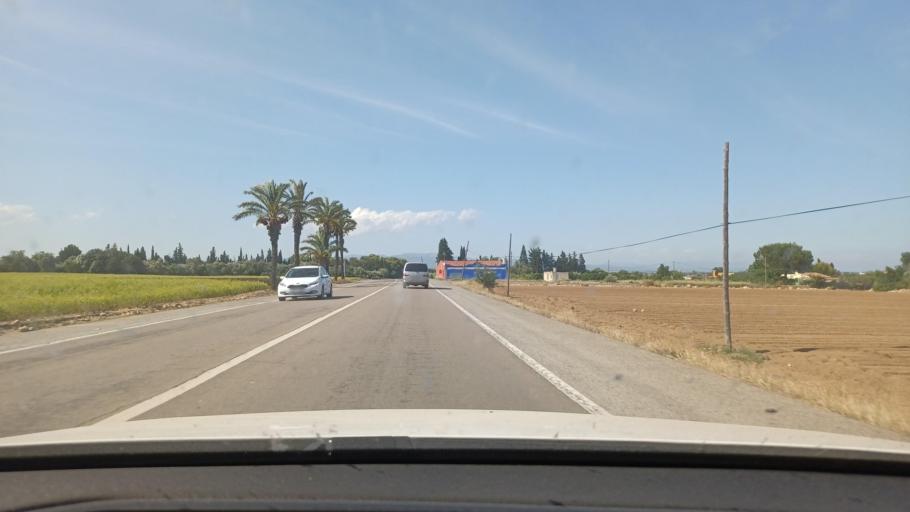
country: ES
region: Catalonia
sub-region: Provincia de Tarragona
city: Amposta
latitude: 40.6701
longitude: 0.5829
